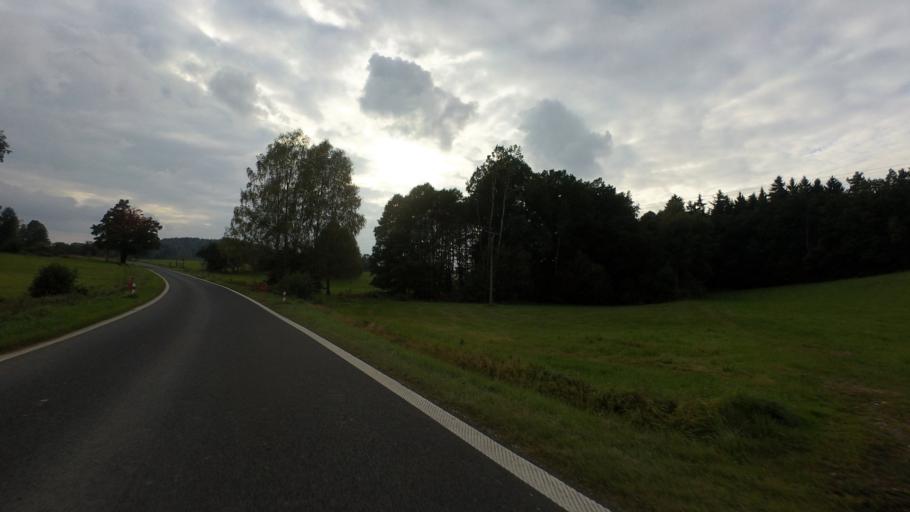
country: CZ
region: Ustecky
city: Dolni Poustevna
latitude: 51.0130
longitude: 14.3026
